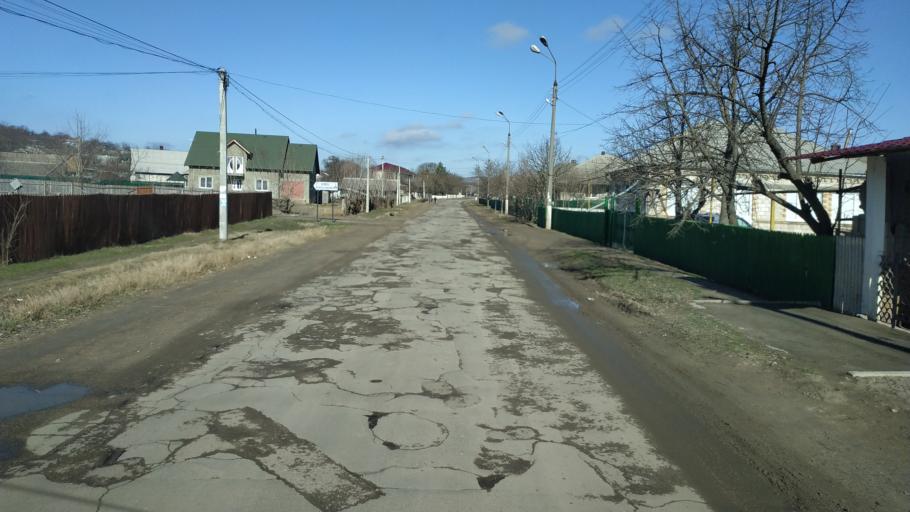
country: MD
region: Hincesti
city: Hincesti
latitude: 46.9584
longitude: 28.6046
